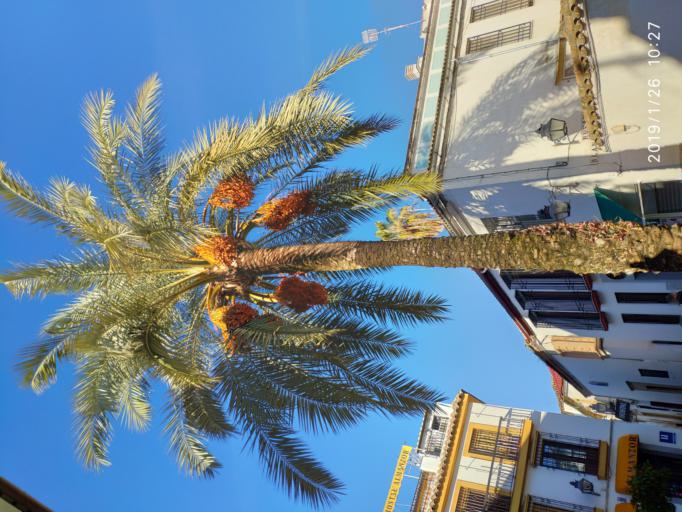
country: ES
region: Andalusia
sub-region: Province of Cordoba
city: Cordoba
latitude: 37.8800
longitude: -4.7759
